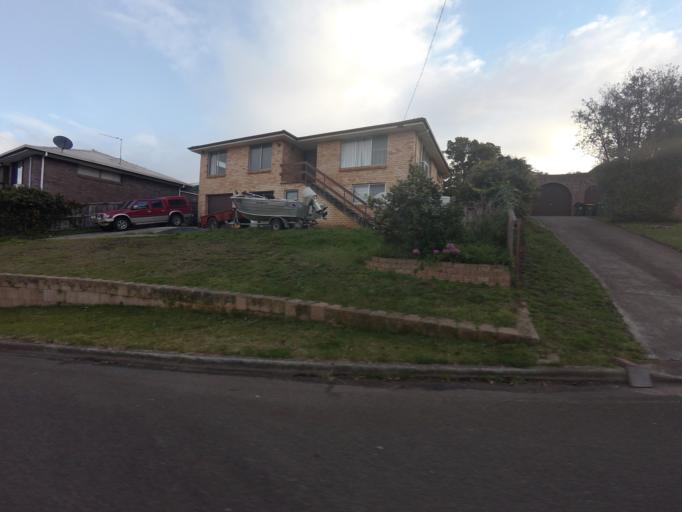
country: AU
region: Tasmania
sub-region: Clarence
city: Rokeby
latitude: -42.8939
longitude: 147.4298
